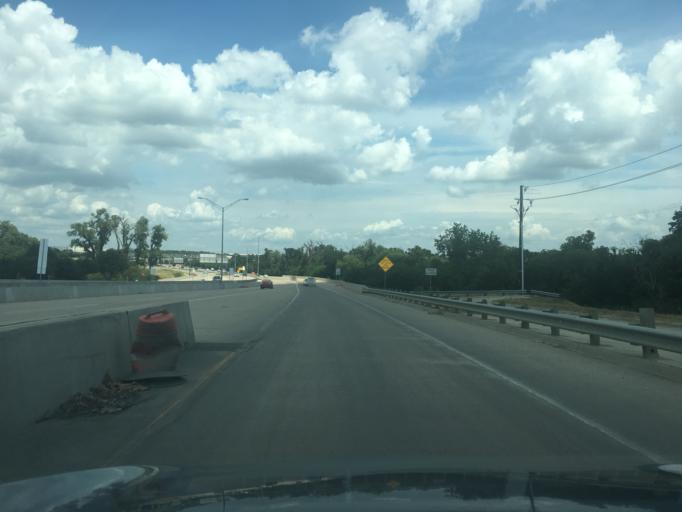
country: US
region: Texas
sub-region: Dallas County
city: Coppell
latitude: 32.9761
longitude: -97.0363
